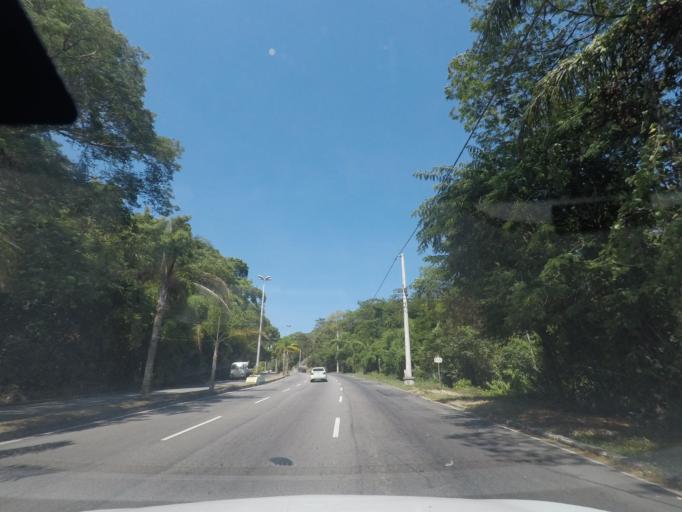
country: BR
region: Rio de Janeiro
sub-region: Niteroi
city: Niteroi
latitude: -22.9235
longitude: -43.0579
